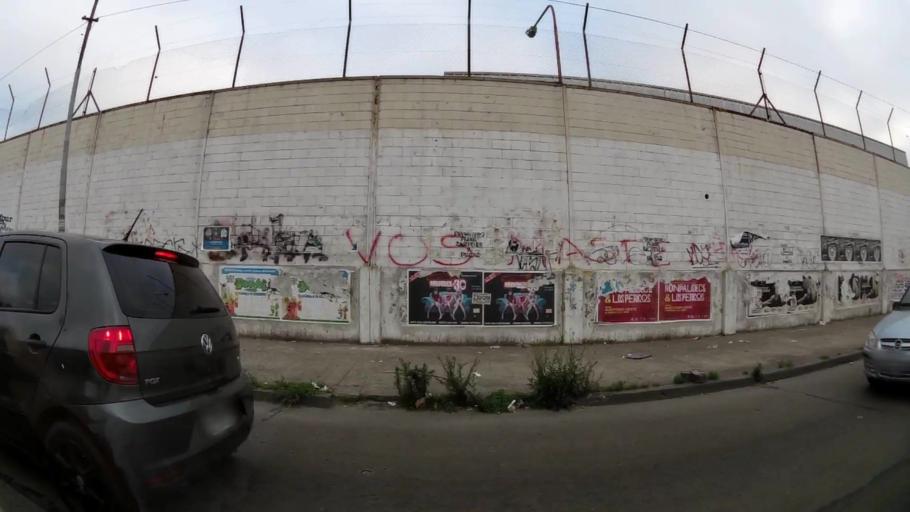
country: AR
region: Buenos Aires
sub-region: Partido de Moron
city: Moron
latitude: -34.6634
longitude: -58.5975
